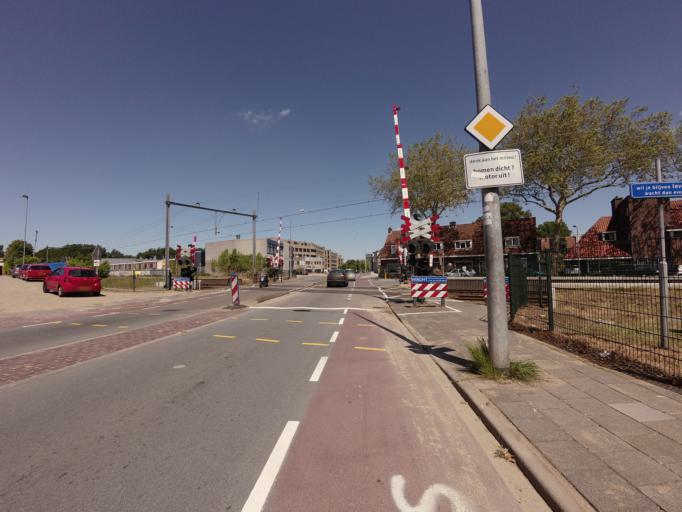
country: NL
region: North Holland
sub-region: Gemeente Hilversum
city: Hilversum
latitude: 52.2200
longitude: 5.1947
